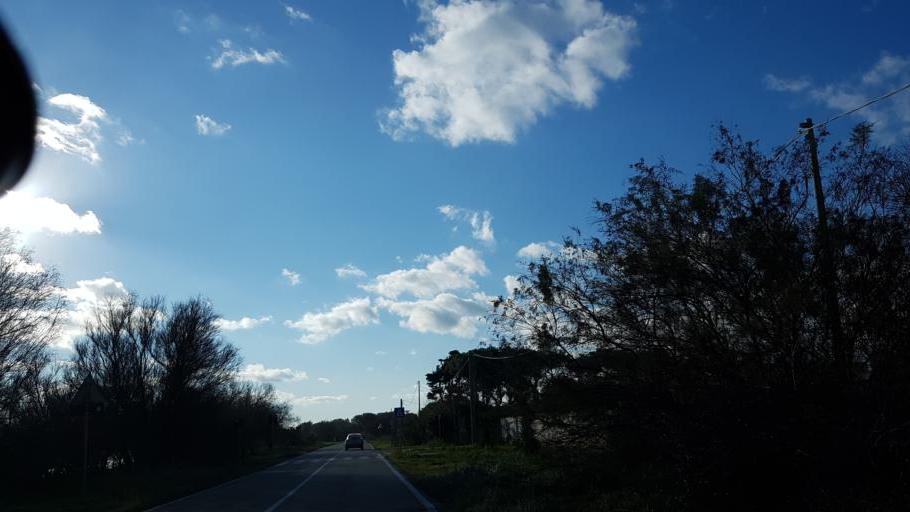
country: IT
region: Apulia
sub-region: Provincia di Brindisi
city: Materdomini
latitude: 40.6723
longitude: 17.9457
